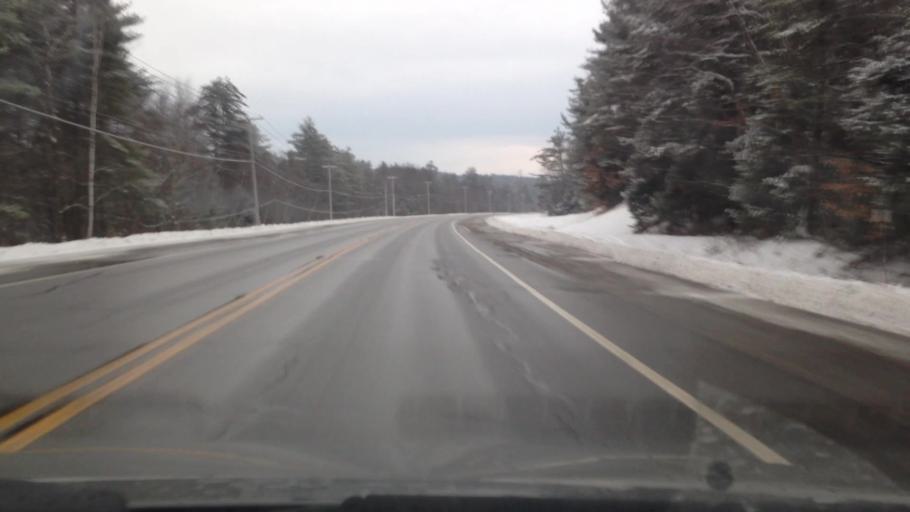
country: US
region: New Hampshire
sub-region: Cheshire County
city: Keene
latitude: 42.9821
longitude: -72.2571
